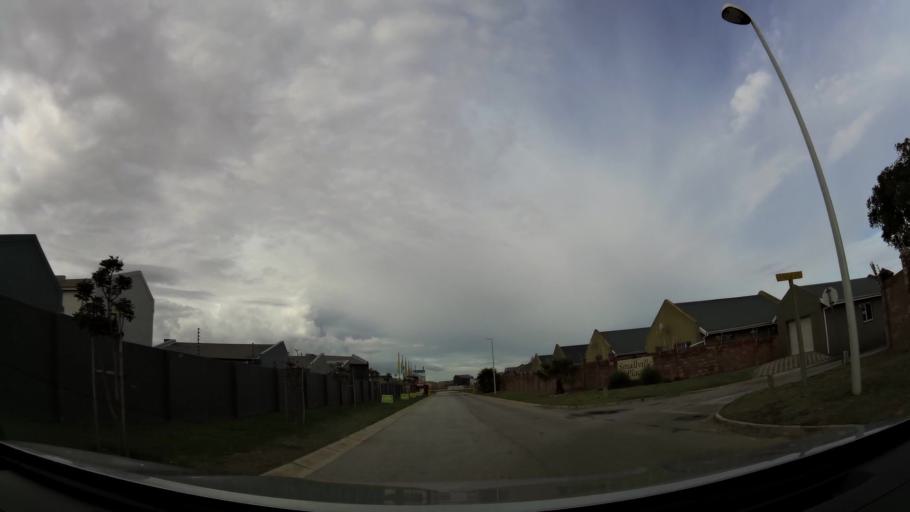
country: ZA
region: Eastern Cape
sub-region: Nelson Mandela Bay Metropolitan Municipality
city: Port Elizabeth
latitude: -33.9317
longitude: 25.4675
